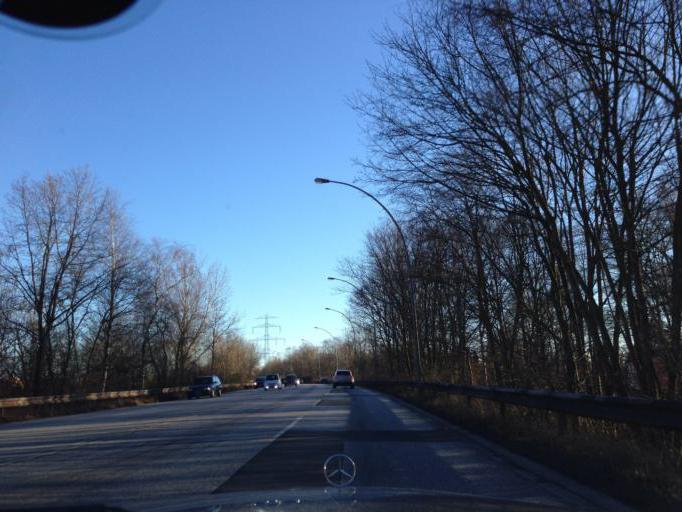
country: DE
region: Schleswig-Holstein
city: Stapelfeld
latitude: 53.6117
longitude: 10.1776
